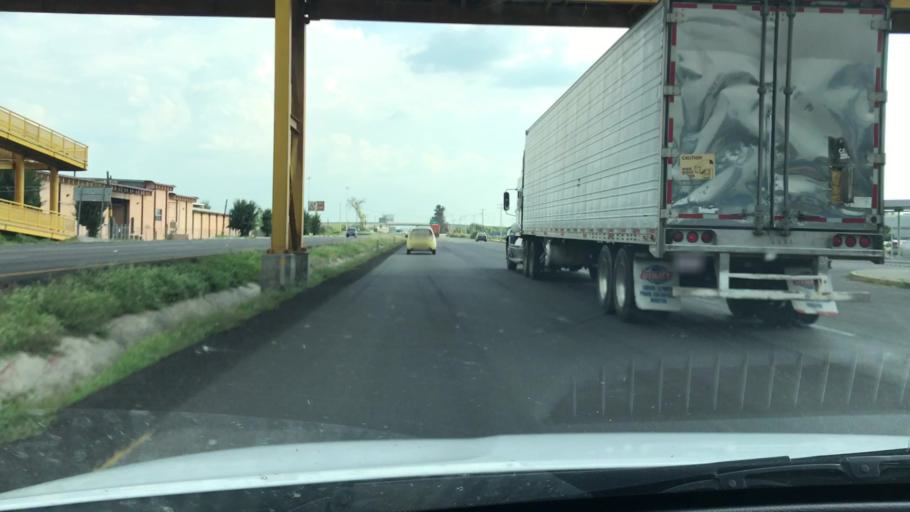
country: MX
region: Guanajuato
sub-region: Irapuato
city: Colonia Morelos de Guadalupe de Rivera
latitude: 20.5977
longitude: -101.4195
